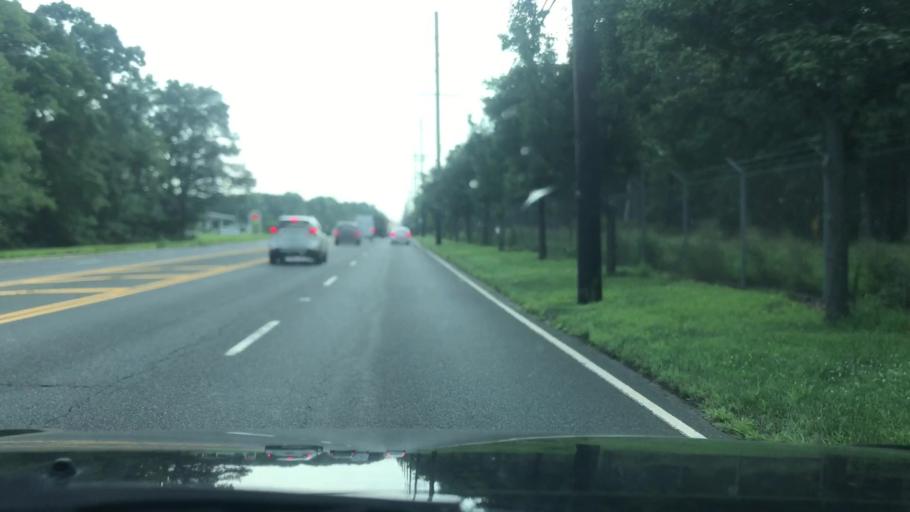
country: US
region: New Jersey
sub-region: Monmouth County
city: Tinton Falls
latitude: 40.2601
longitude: -74.0903
